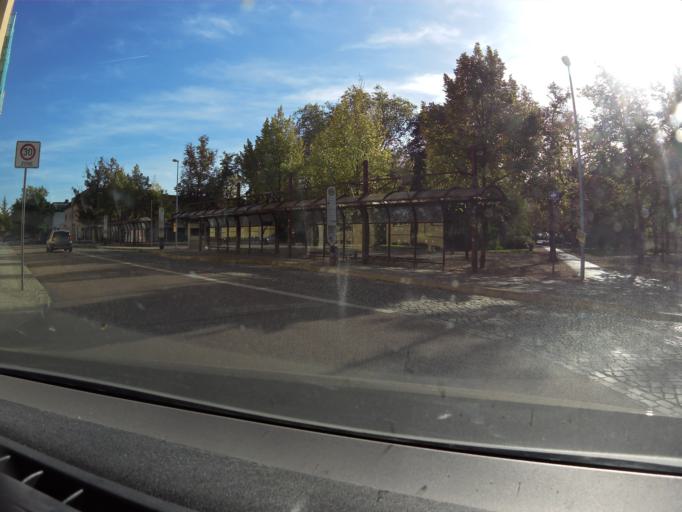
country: DE
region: Saxony-Anhalt
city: Bernburg
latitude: 51.7956
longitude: 11.7444
